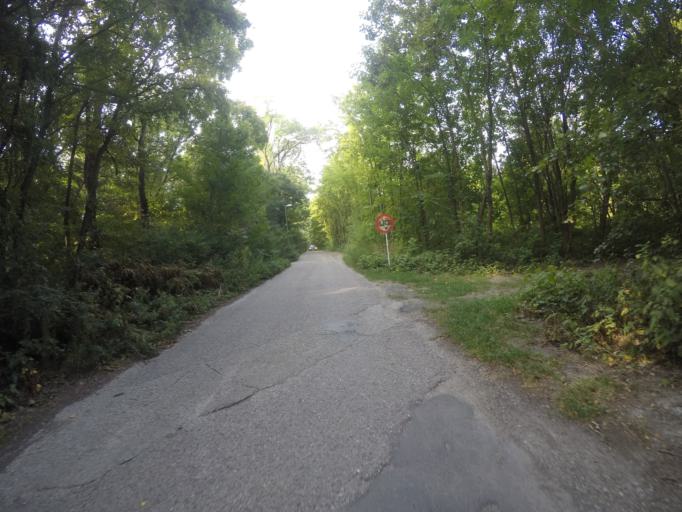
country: SK
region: Trnavsky
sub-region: Okres Dunajska Streda
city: Velky Meder
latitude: 47.8501
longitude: 17.7611
